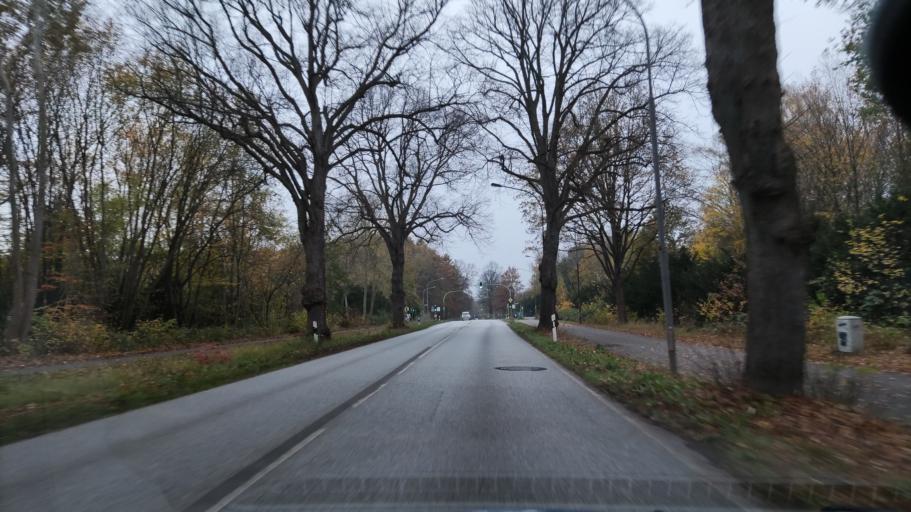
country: DE
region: Schleswig-Holstein
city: Gross Gronau
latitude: 53.8298
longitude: 10.7183
